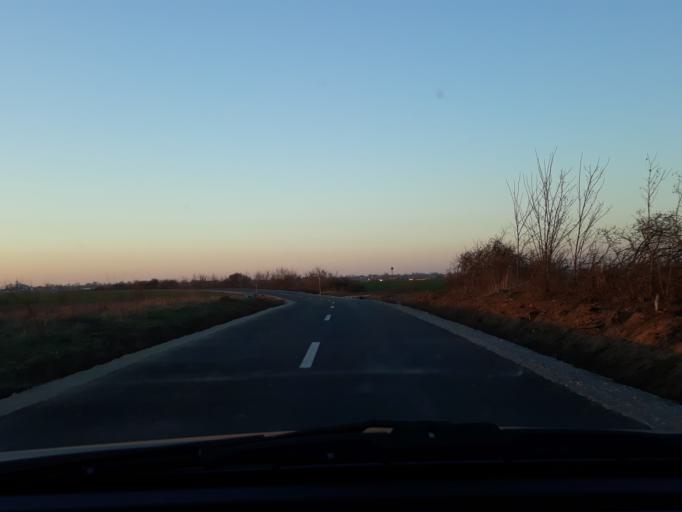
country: RO
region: Bihor
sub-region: Comuna Gepiu
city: Gepiu
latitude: 46.9160
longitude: 21.7877
